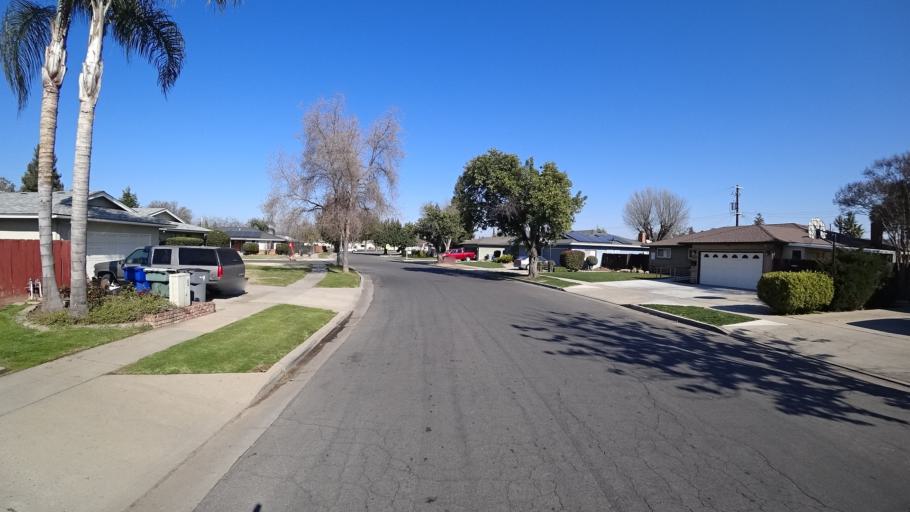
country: US
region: California
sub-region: Fresno County
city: Clovis
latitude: 36.8275
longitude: -119.7764
